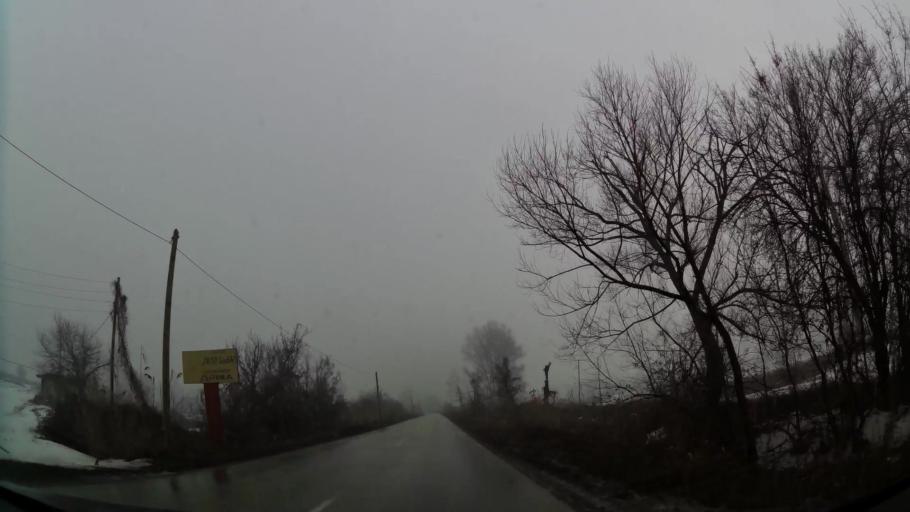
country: MK
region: Ilinden
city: Idrizovo
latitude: 41.9478
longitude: 21.5922
